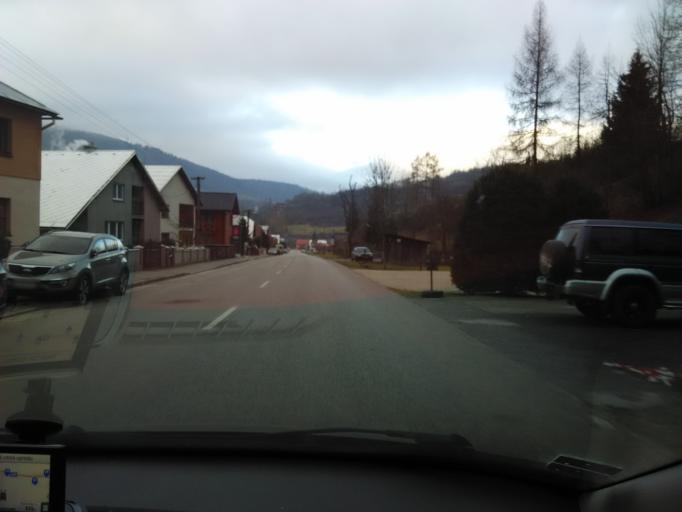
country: SK
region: Zilinsky
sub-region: Okres Zilina
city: Terchova
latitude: 49.2522
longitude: 19.0375
